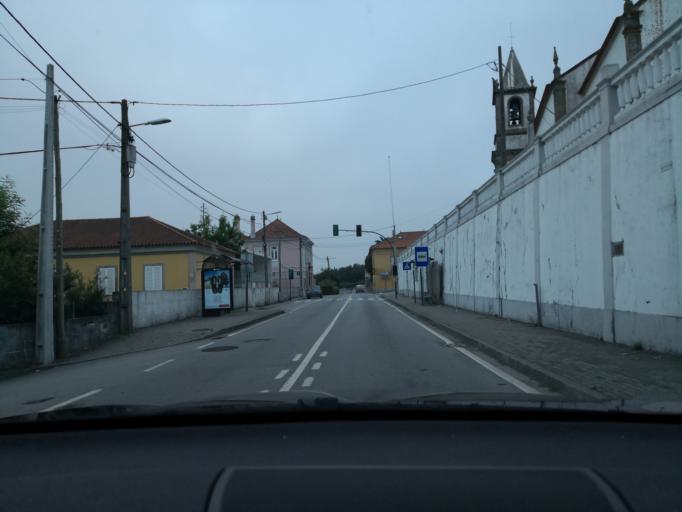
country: PT
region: Aveiro
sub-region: Santa Maria da Feira
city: Lamas
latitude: 41.0016
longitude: -8.5651
